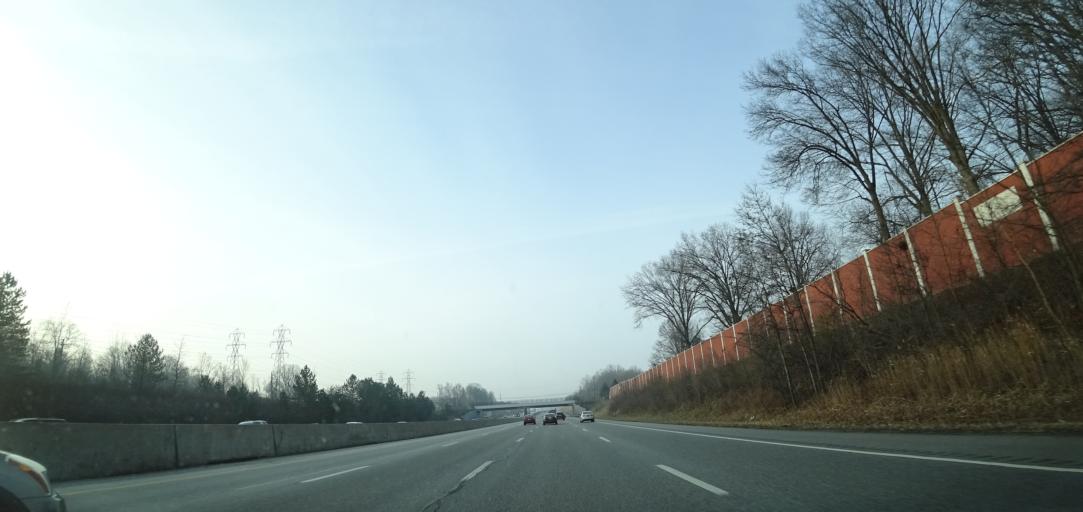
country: US
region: Ohio
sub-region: Cuyahoga County
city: Independence
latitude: 41.3870
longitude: -81.6531
